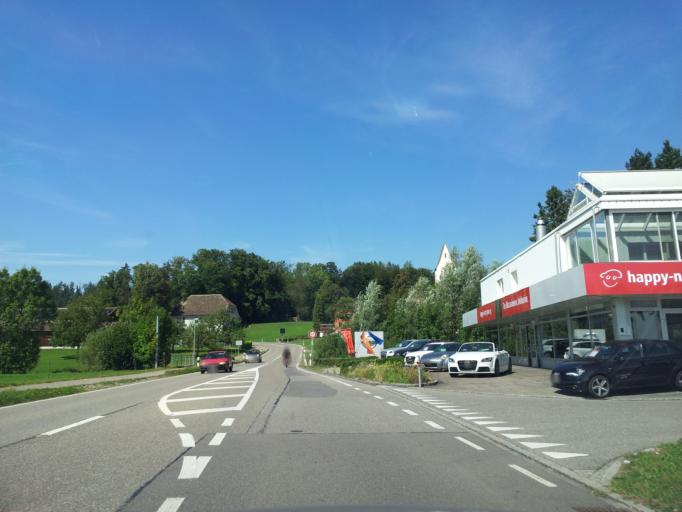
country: CH
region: Saint Gallen
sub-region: Wahlkreis See-Gaster
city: Jona
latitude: 47.2261
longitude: 8.8619
